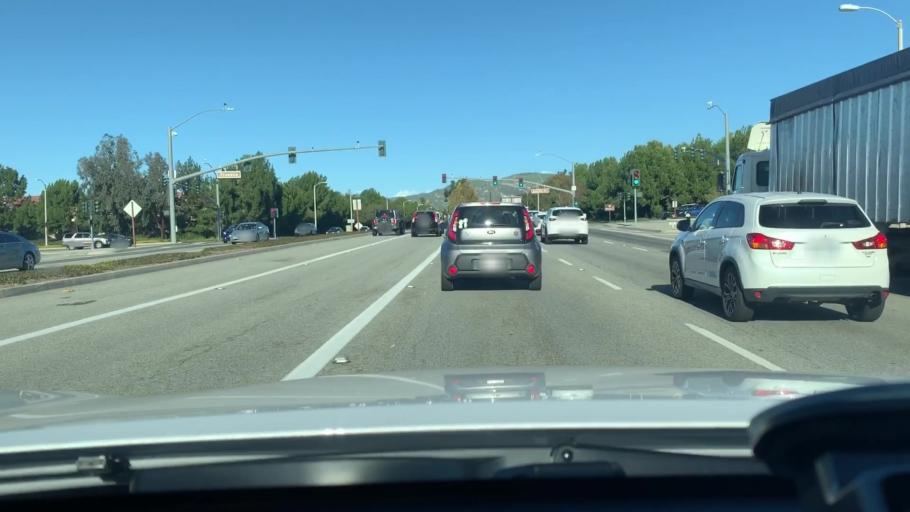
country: US
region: California
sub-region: Orange County
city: Lake Forest
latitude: 33.6864
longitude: -117.7493
